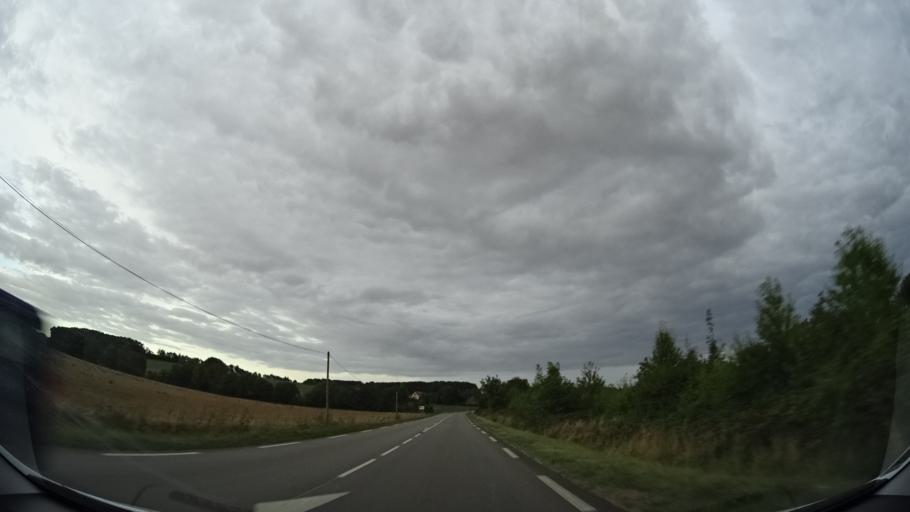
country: FR
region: Centre
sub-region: Departement du Loiret
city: Douchy
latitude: 47.9352
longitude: 3.0890
